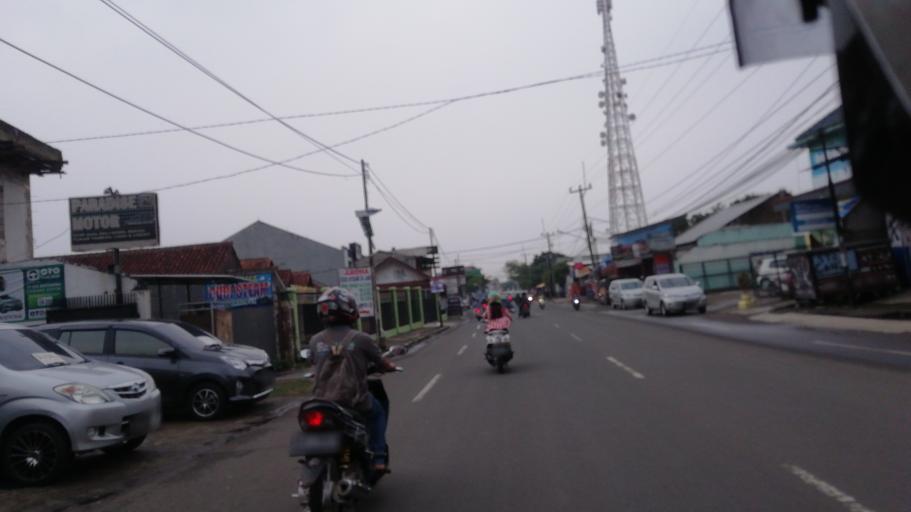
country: ID
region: West Java
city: Cibinong
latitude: -6.5036
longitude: 106.8081
